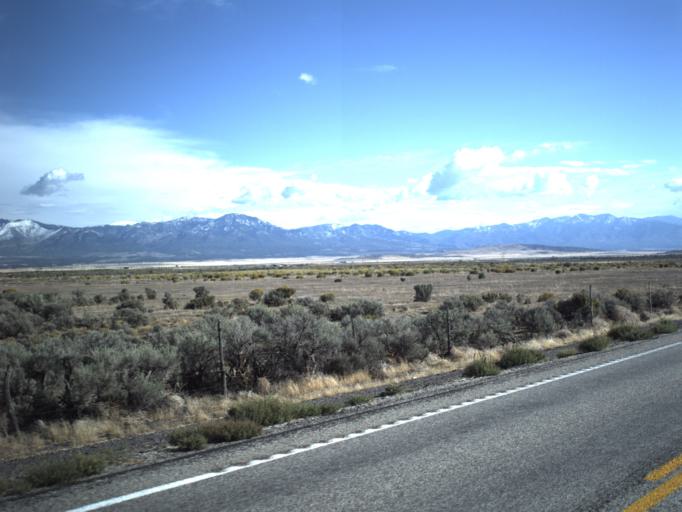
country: US
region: Utah
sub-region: Millard County
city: Fillmore
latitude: 39.1665
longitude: -112.4101
